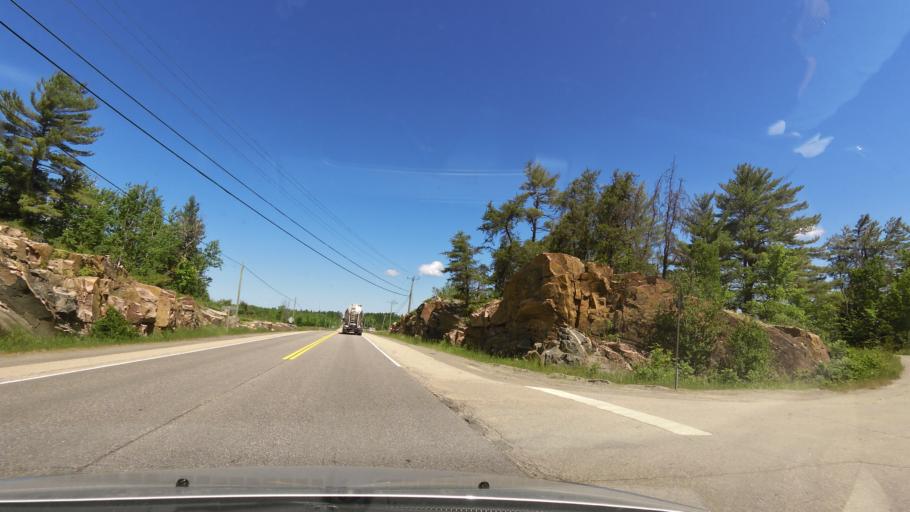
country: CA
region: Ontario
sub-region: Parry Sound District
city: Parry Sound
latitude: 45.8056
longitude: -80.5391
